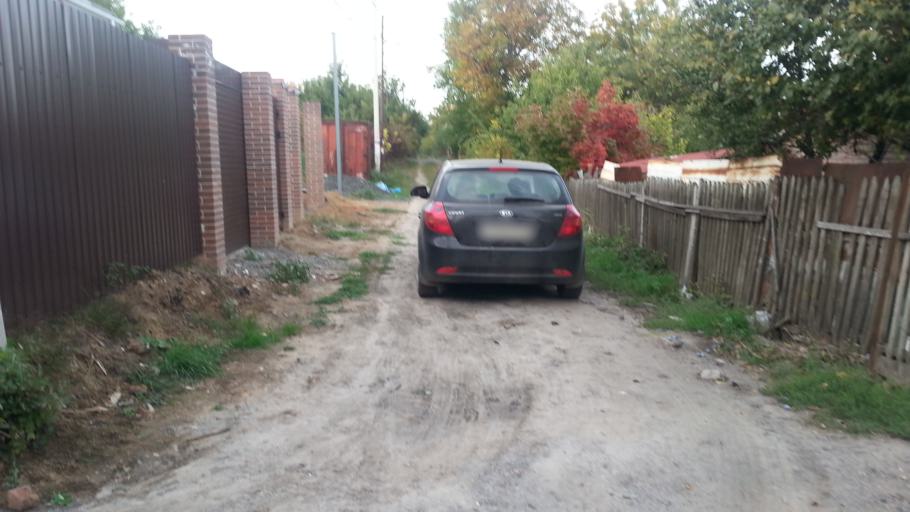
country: RU
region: Rostov
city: Severnyy
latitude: 47.2912
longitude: 39.6733
